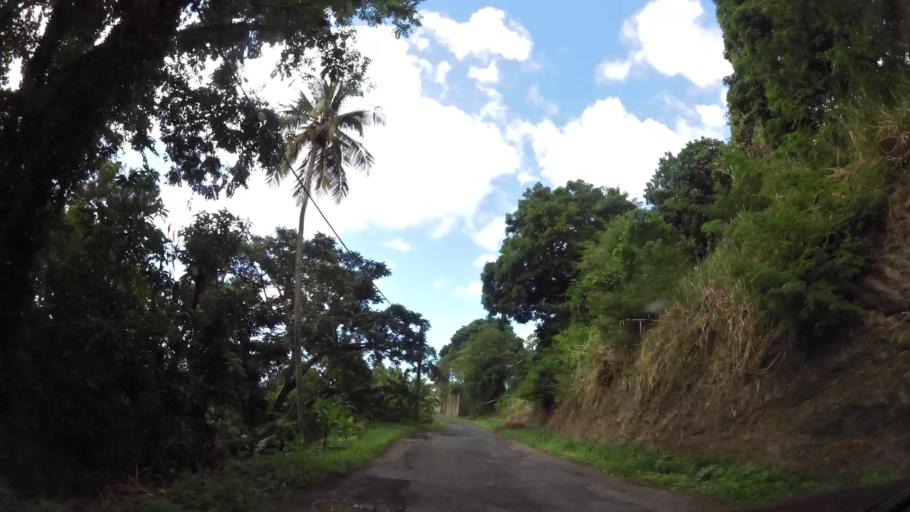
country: DM
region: Saint John
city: Portsmouth
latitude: 15.6233
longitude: -61.4630
